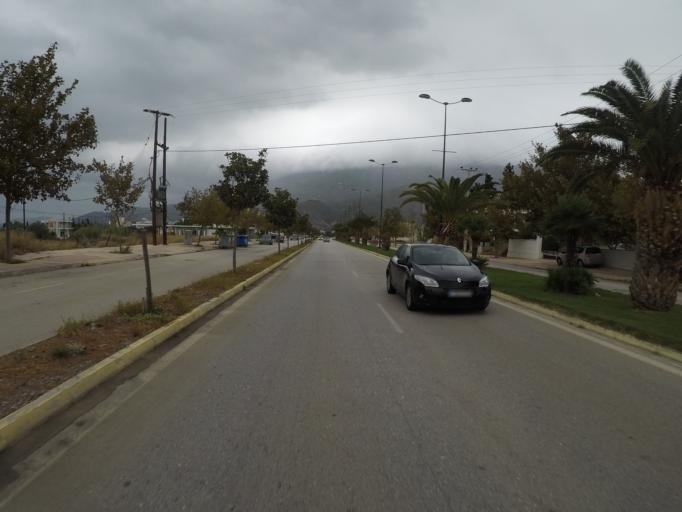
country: GR
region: Peloponnese
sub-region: Nomos Korinthias
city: Loutraki
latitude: 37.9594
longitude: 22.9790
